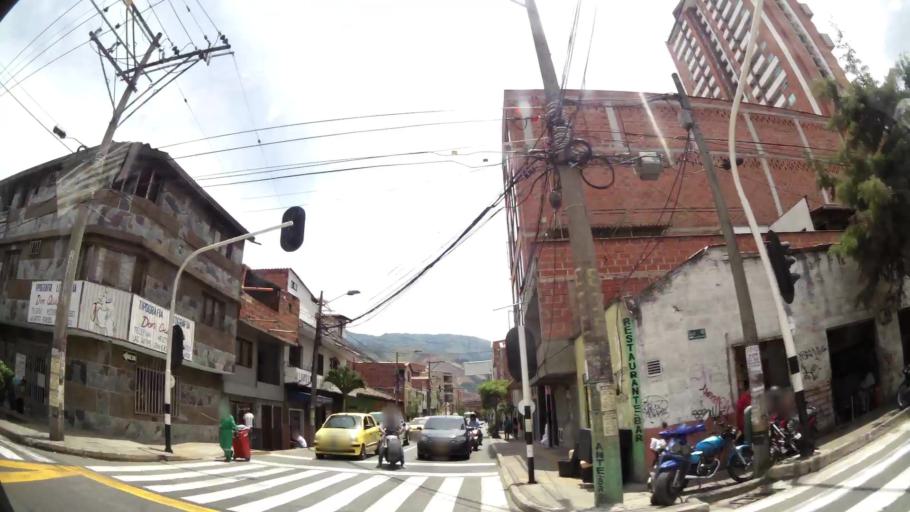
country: CO
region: Antioquia
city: Bello
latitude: 6.3324
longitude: -75.5558
